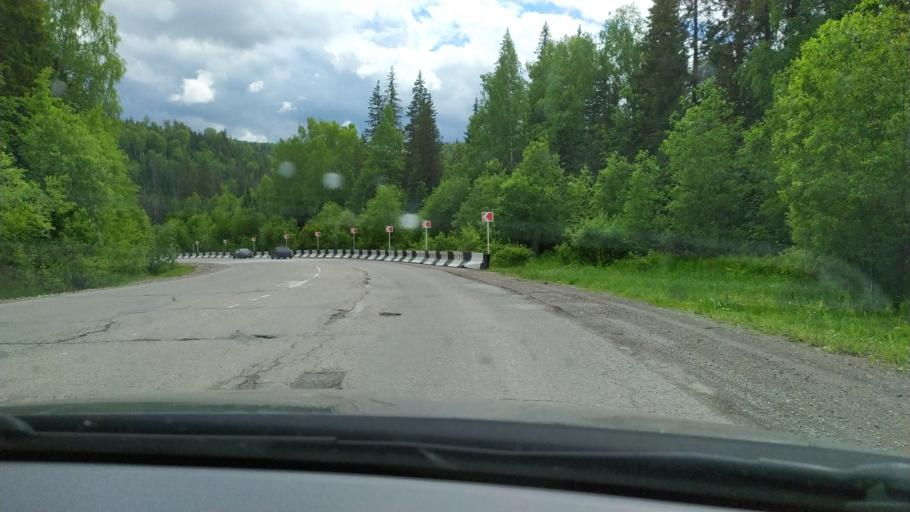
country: RU
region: Perm
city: Gremyachinsk
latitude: 58.4431
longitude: 57.8666
